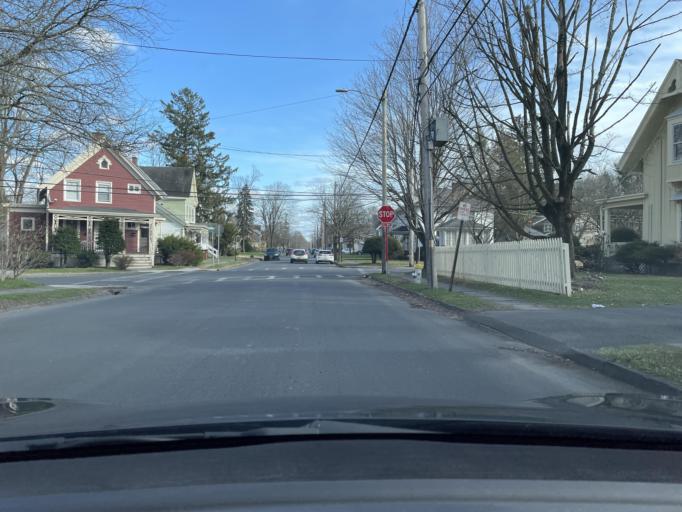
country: US
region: New York
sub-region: Ulster County
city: Kingston
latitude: 41.9302
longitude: -74.0212
